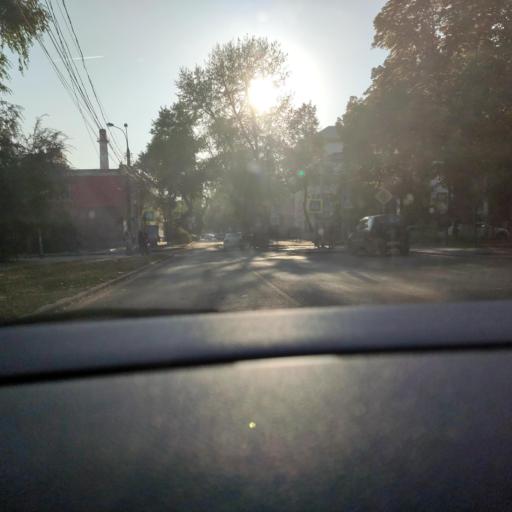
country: RU
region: Voronezj
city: Voronezh
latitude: 51.6727
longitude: 39.1960
